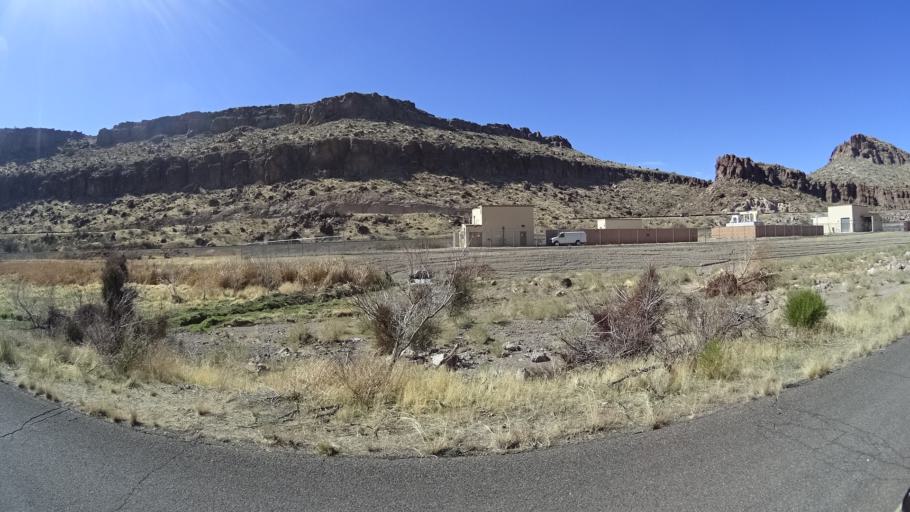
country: US
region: Arizona
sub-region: Mohave County
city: Kingman
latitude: 35.1761
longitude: -114.0620
